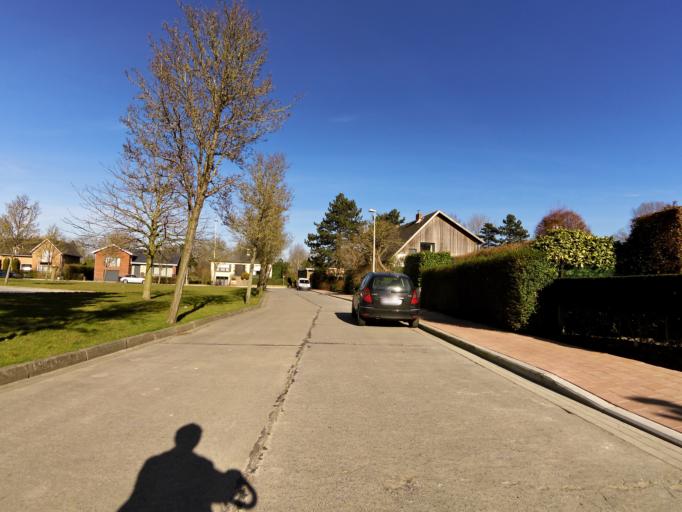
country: BE
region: Flanders
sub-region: Provincie West-Vlaanderen
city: Ostend
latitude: 51.2111
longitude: 2.9331
